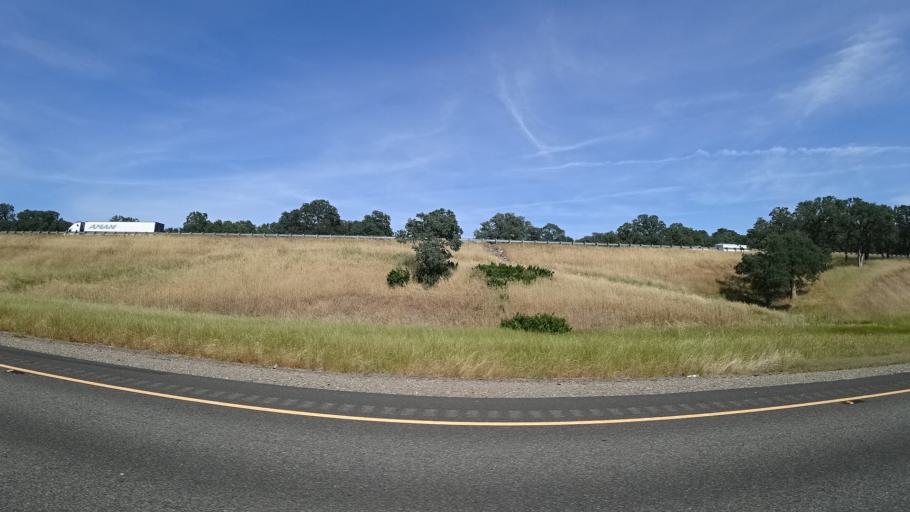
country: US
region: California
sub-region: Tehama County
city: Red Bluff
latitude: 40.2155
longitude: -122.2502
